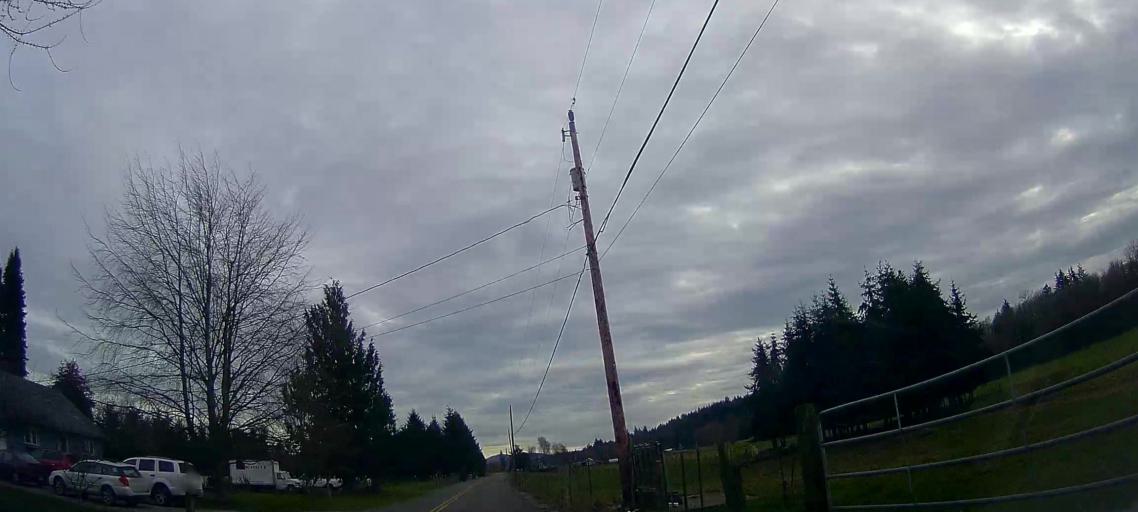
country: US
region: Washington
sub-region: Skagit County
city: Burlington
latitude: 48.5133
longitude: -122.4297
